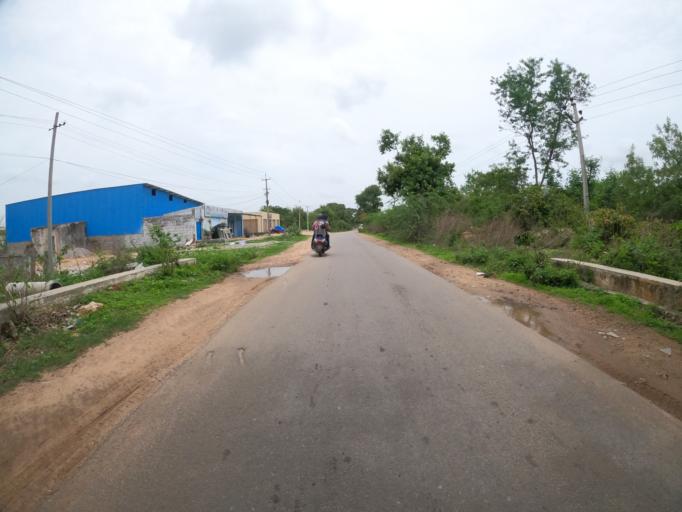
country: IN
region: Telangana
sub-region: Hyderabad
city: Hyderabad
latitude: 17.3403
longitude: 78.3703
